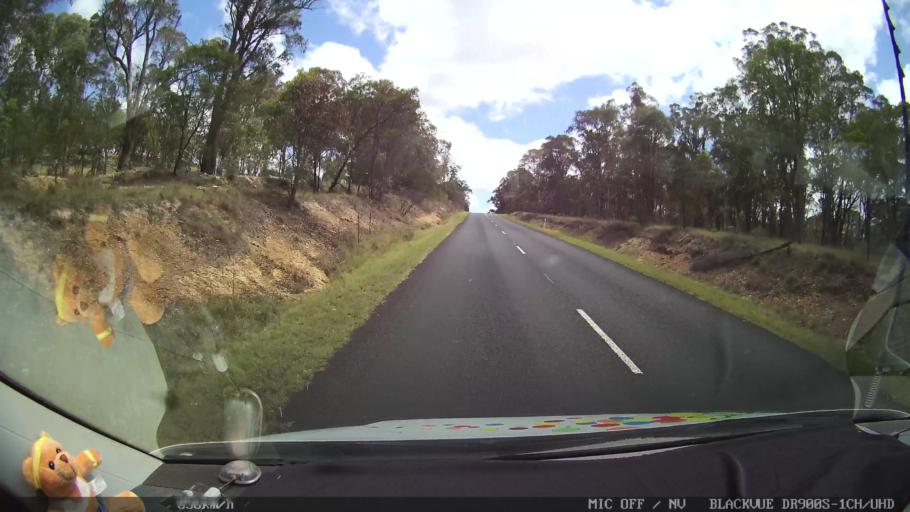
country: AU
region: New South Wales
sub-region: Glen Innes Severn
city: Glen Innes
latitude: -29.5941
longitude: 151.6661
